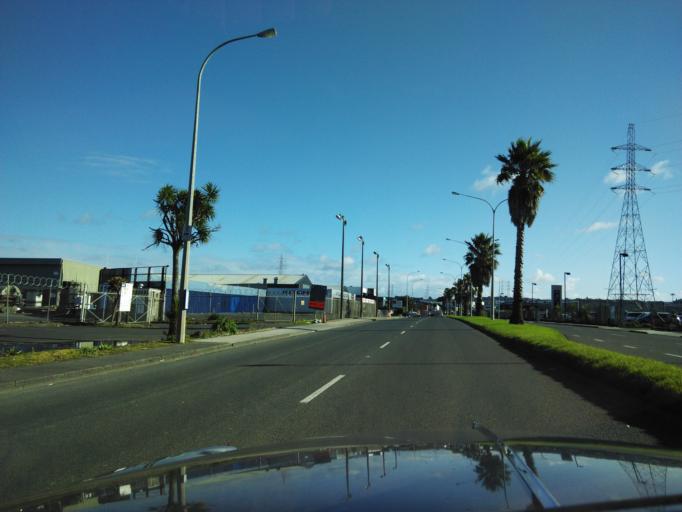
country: NZ
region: Auckland
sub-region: Auckland
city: Mangere
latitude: -36.9264
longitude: 174.7921
